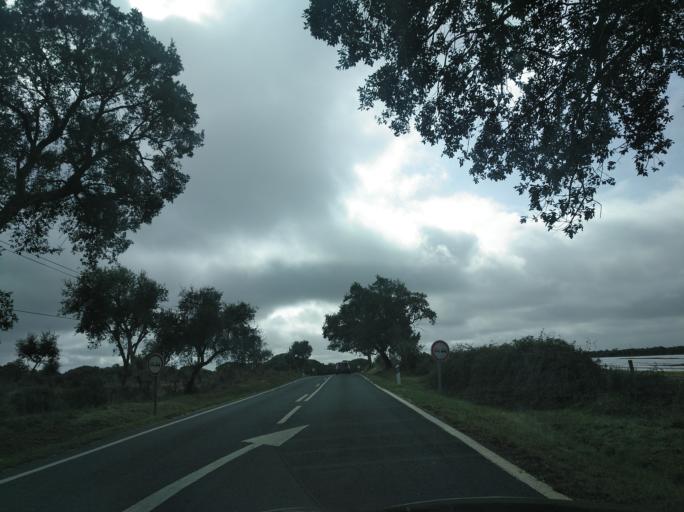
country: PT
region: Setubal
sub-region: Santiago do Cacem
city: Santo Andre
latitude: 38.1155
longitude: -8.7449
